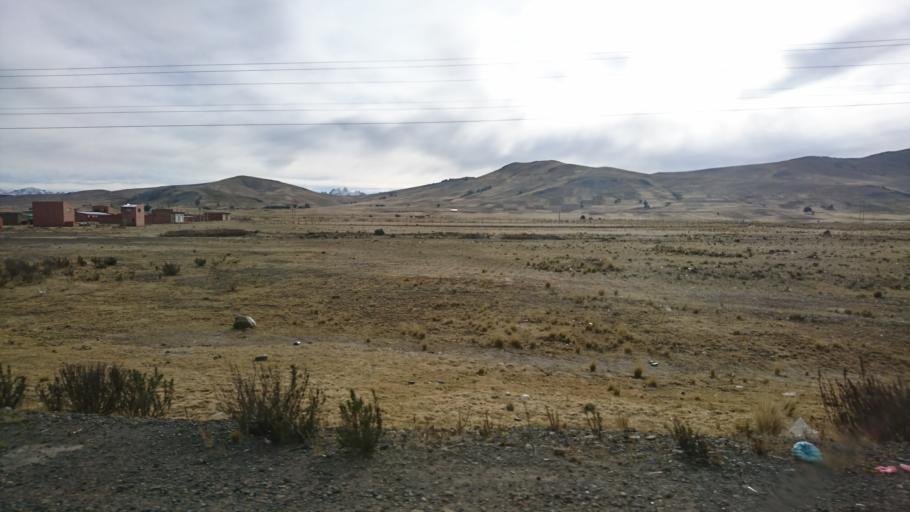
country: BO
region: La Paz
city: Batallas
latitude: -16.3808
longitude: -68.3764
